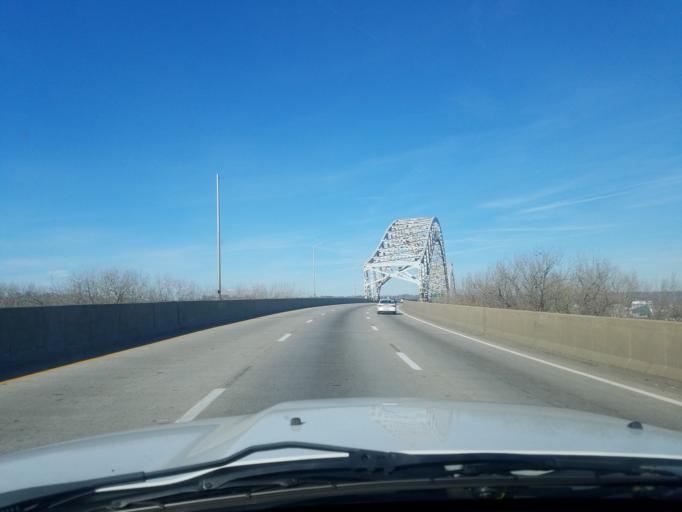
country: US
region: Indiana
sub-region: Floyd County
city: New Albany
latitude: 38.2759
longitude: -85.8188
